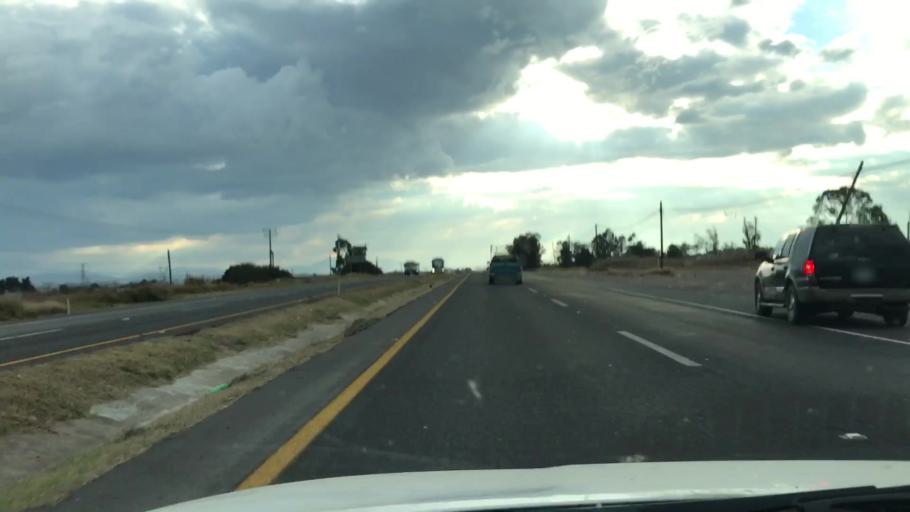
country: MX
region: Guanajuato
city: Penjamo
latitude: 20.4119
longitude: -101.7345
